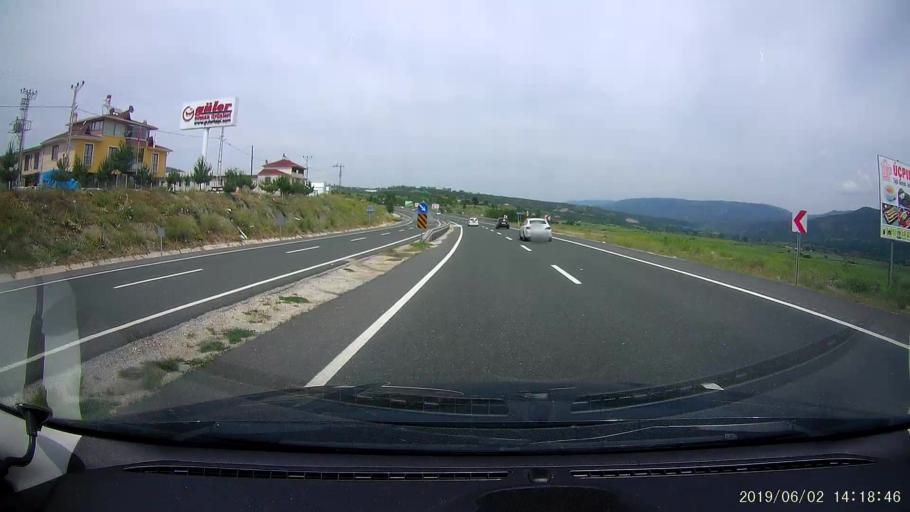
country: TR
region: Kastamonu
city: Tosya
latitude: 40.9568
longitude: 33.9635
